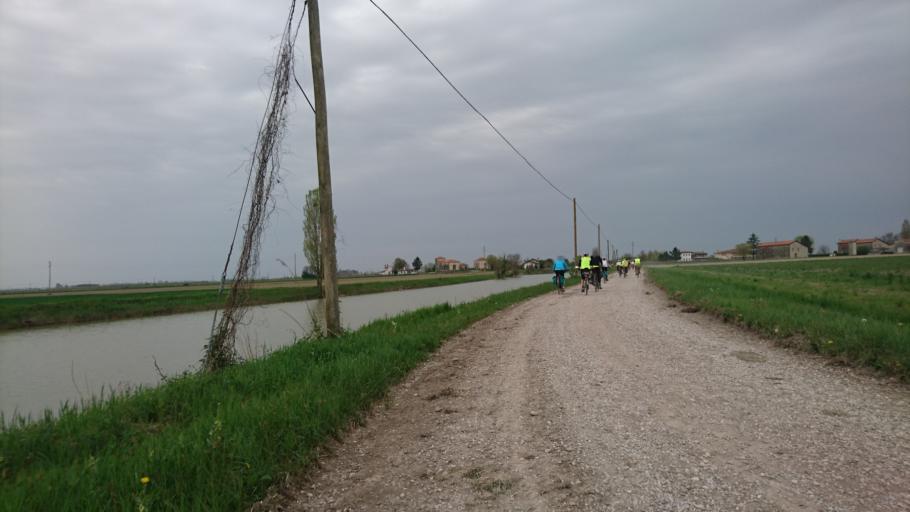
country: IT
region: Veneto
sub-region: Provincia di Venezia
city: Lugugnana
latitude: 45.6878
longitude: 12.9427
